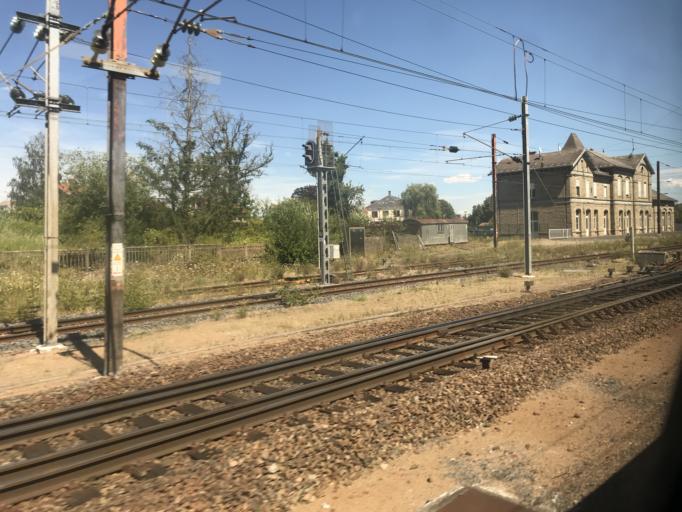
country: FR
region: Lorraine
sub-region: Departement de la Moselle
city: Reding
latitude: 48.7429
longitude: 7.0944
